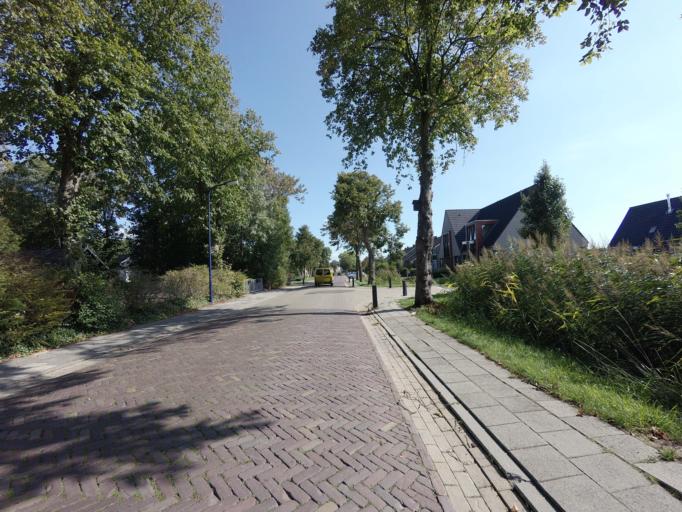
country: NL
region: Friesland
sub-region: Gemeente Littenseradiel
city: Makkum
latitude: 53.1008
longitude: 5.6440
